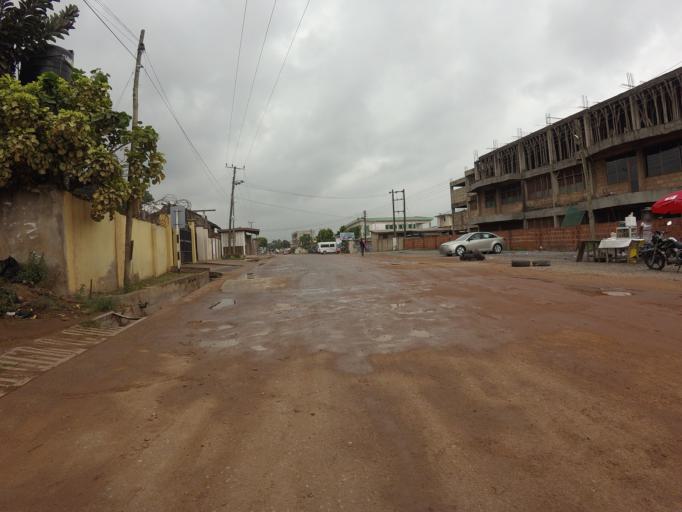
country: GH
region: Greater Accra
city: Dome
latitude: 5.6338
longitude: -0.2332
